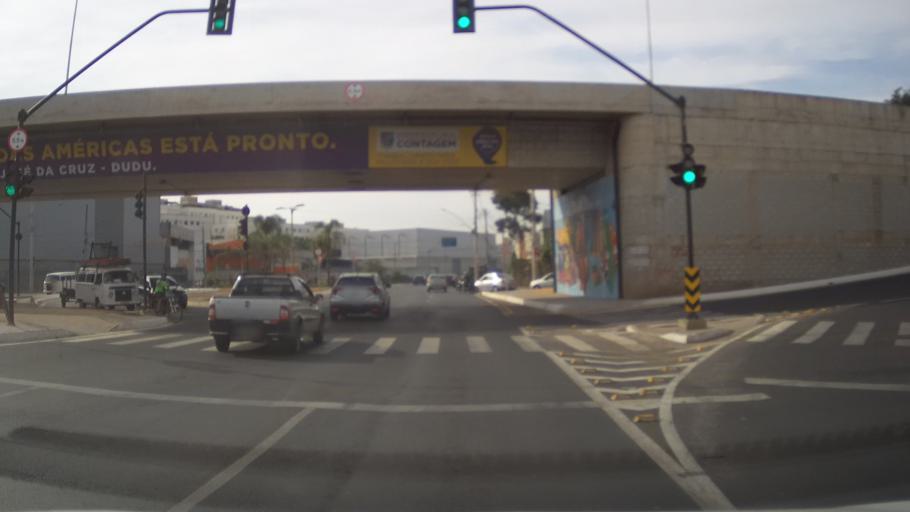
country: BR
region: Minas Gerais
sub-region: Contagem
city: Contagem
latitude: -19.8854
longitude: -44.0389
